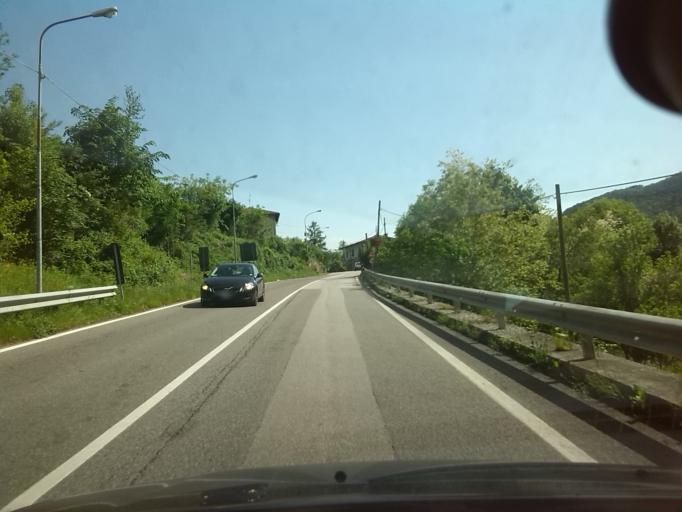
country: IT
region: Friuli Venezia Giulia
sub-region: Provincia di Udine
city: Pulfero
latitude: 46.1550
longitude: 13.4886
